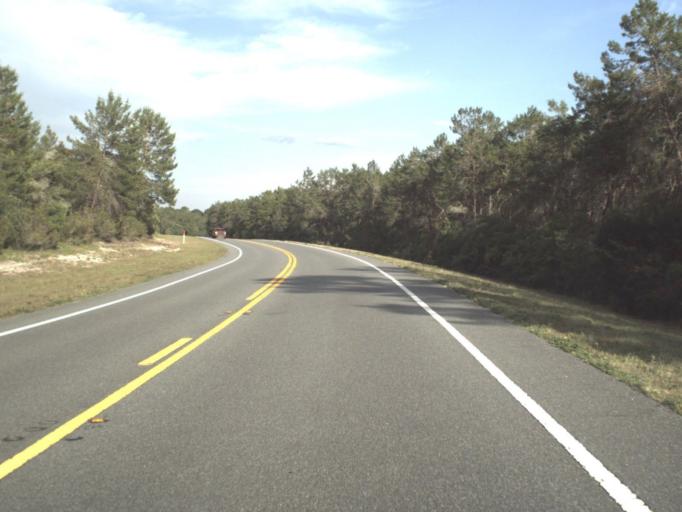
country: US
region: Florida
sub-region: Lake County
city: Astor
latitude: 29.1678
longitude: -81.6159
